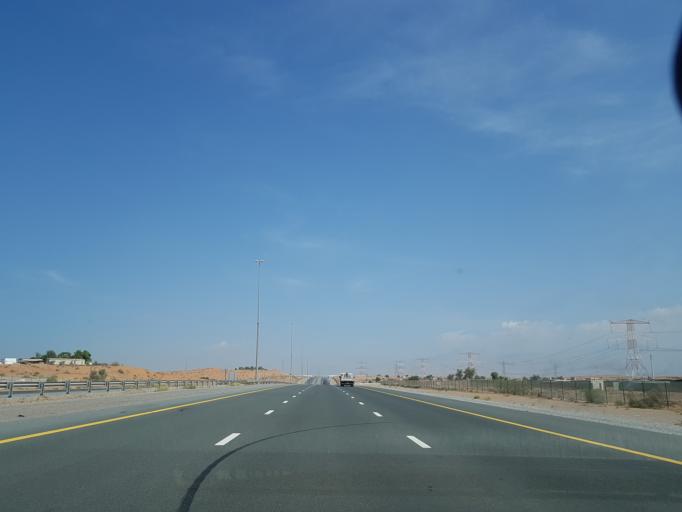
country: AE
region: Ra's al Khaymah
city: Ras al-Khaimah
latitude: 25.6822
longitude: 55.9080
